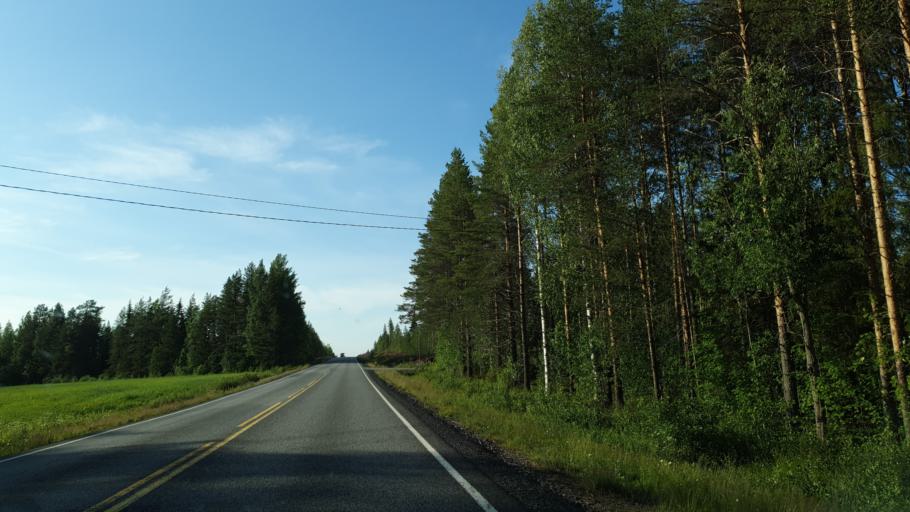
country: FI
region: Kainuu
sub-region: Kehys-Kainuu
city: Kuhmo
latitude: 64.0821
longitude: 29.4851
